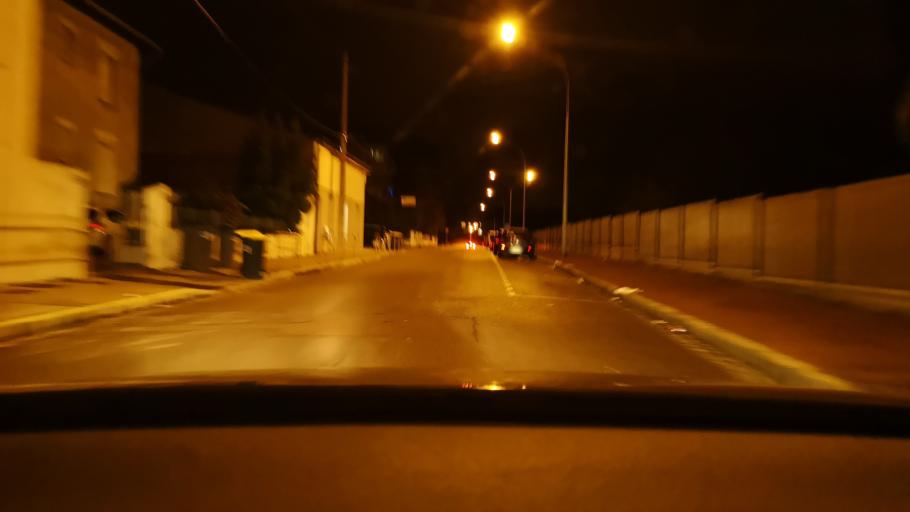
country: FR
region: Bourgogne
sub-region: Departement de Saone-et-Loire
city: Chalon-sur-Saone
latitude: 46.7946
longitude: 4.8580
